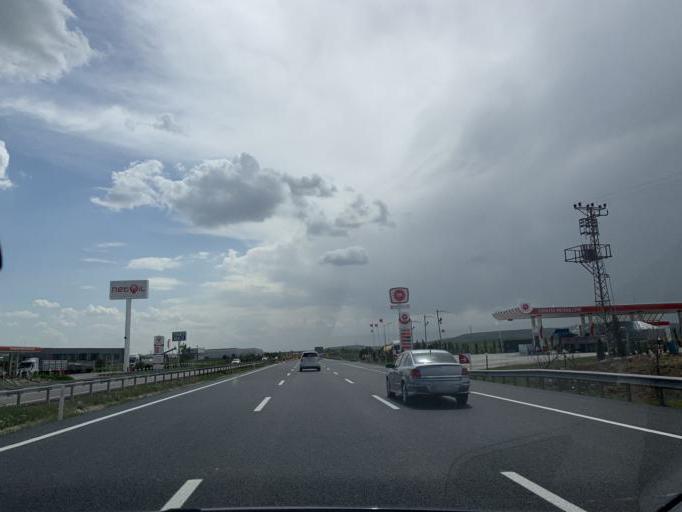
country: TR
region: Ankara
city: Polatli
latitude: 39.6569
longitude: 32.2188
